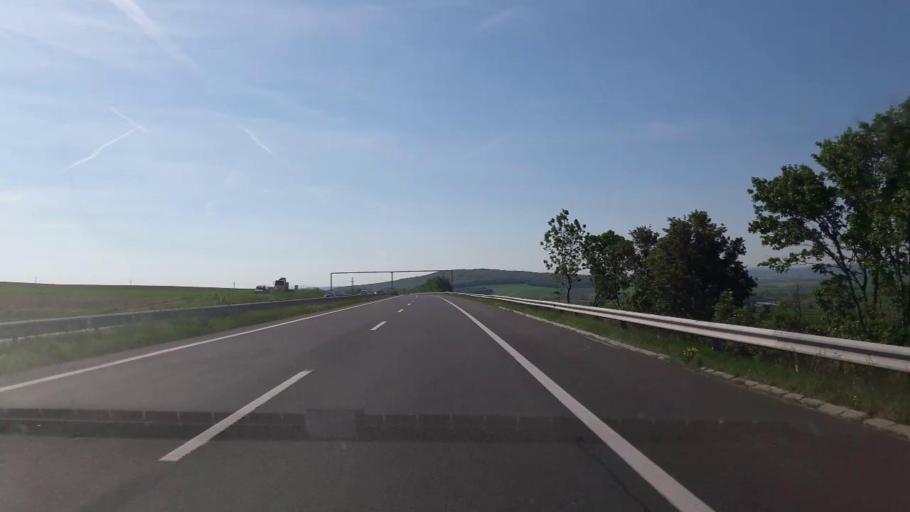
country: AT
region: Burgenland
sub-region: Eisenstadt-Umgebung
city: Steinbrunn
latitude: 47.8445
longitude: 16.4339
